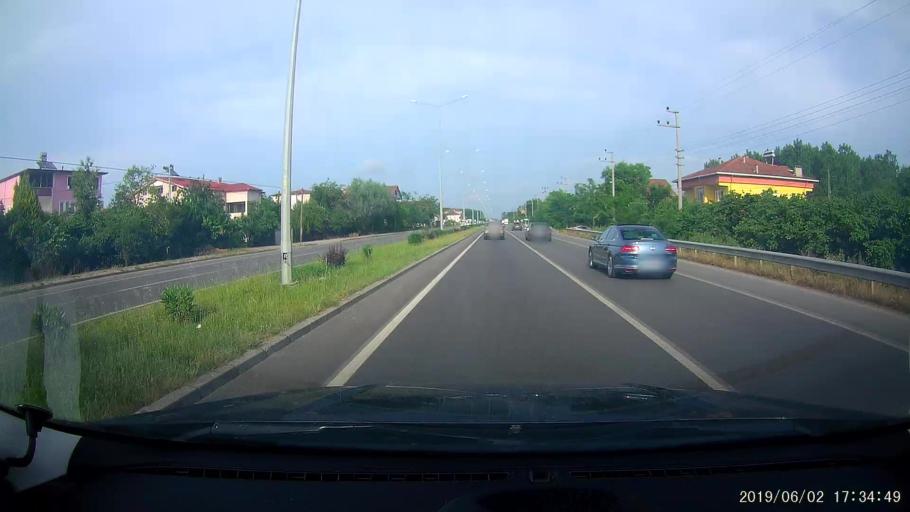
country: TR
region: Samsun
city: Terme
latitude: 41.2199
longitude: 36.8759
